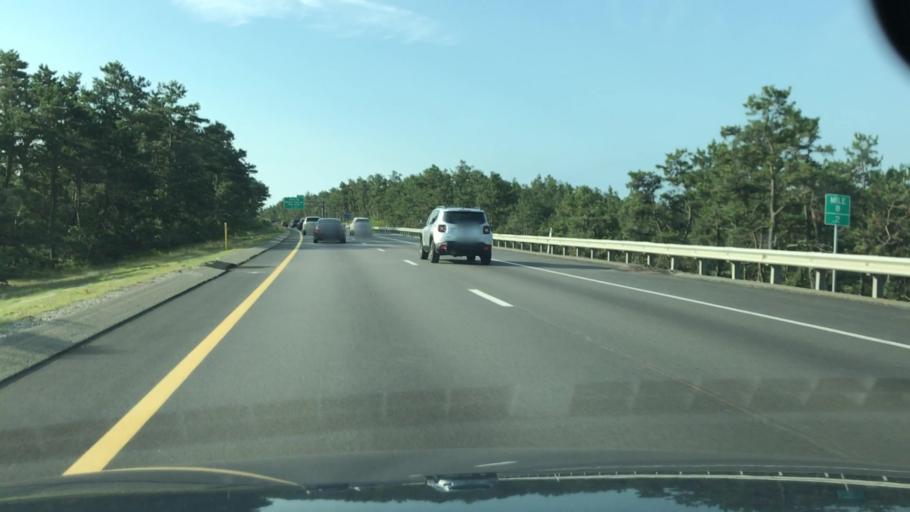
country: US
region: Massachusetts
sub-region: Plymouth County
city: White Island Shores
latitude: 41.8848
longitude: -70.6108
